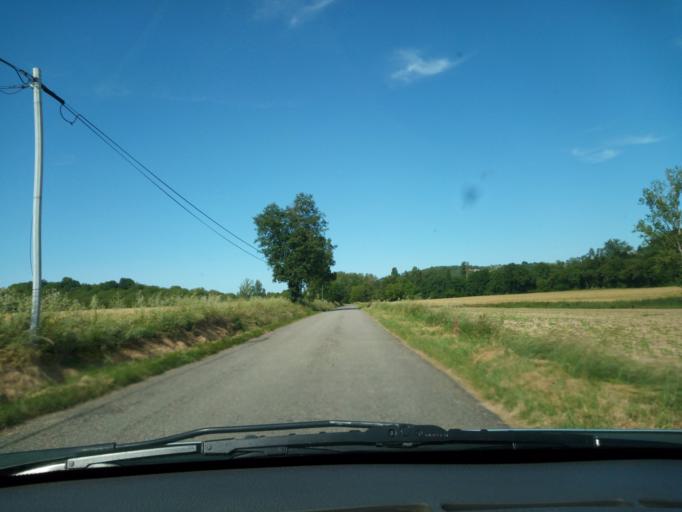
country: FR
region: Midi-Pyrenees
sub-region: Departement du Lot
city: Castelnau-Montratier
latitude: 44.2364
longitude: 1.3356
